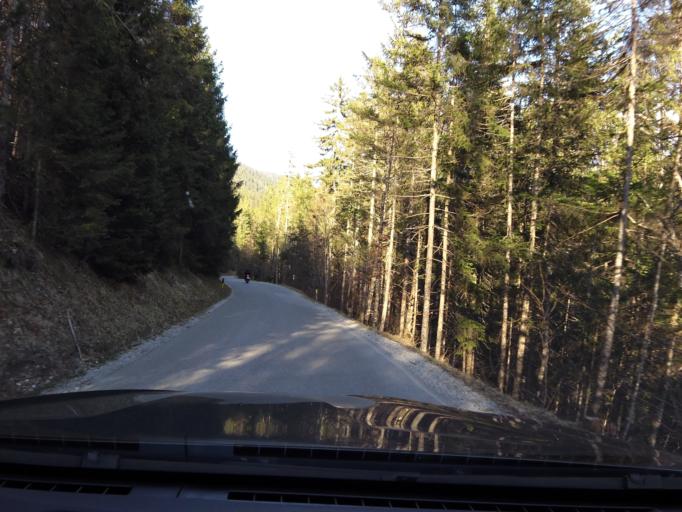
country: DE
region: Bavaria
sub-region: Upper Bavaria
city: Jachenau
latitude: 47.5483
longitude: 11.3814
